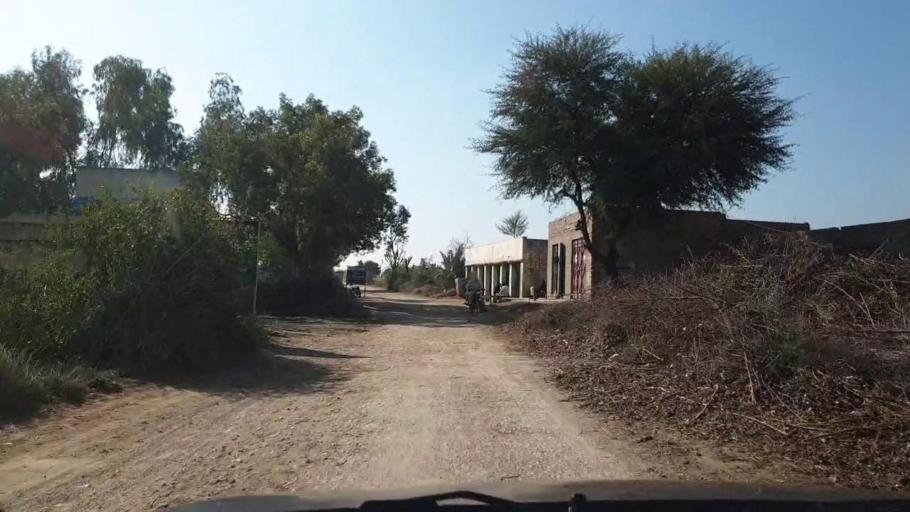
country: PK
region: Sindh
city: Sinjhoro
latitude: 25.9758
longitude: 68.7433
